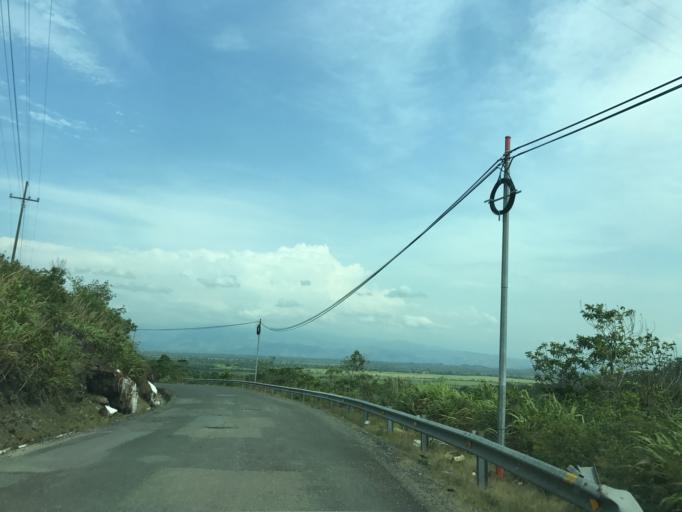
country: GT
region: Izabal
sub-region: Municipio de Los Amates
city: Los Amates
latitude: 15.3876
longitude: -89.0271
